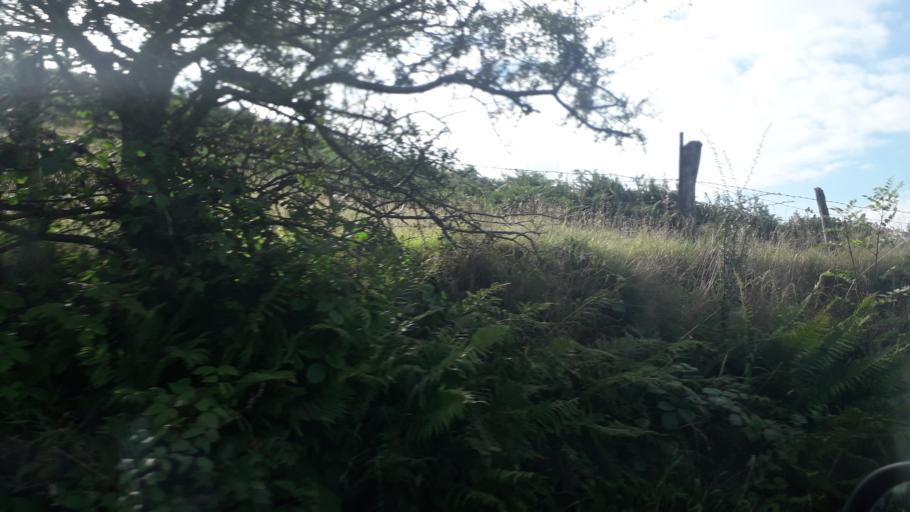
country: GB
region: Northern Ireland
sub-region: Down District
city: Warrenpoint
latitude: 54.0681
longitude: -6.2777
